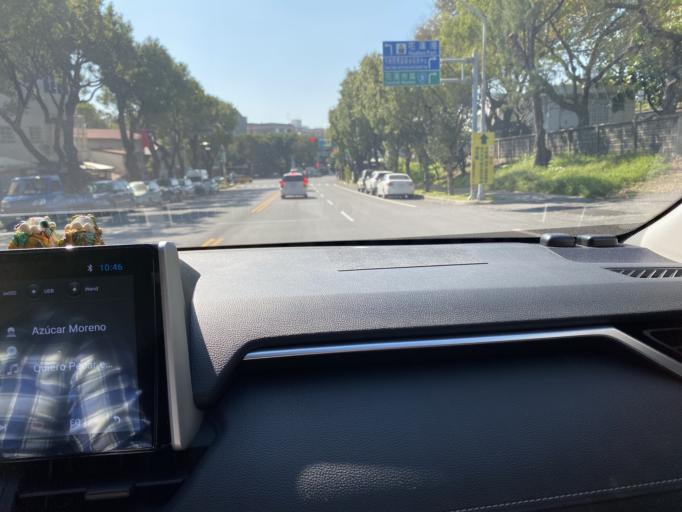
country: TW
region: Taiwan
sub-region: Hualien
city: Hualian
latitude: 23.9867
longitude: 121.6210
